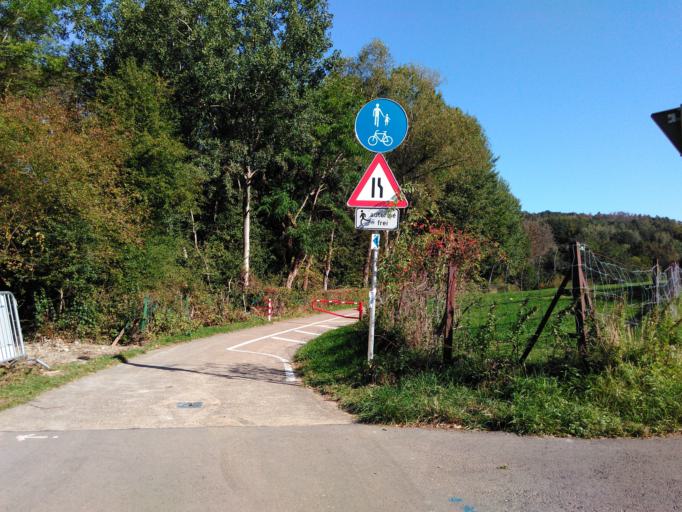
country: LU
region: Luxembourg
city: Eischen
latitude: 49.6862
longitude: 5.8844
